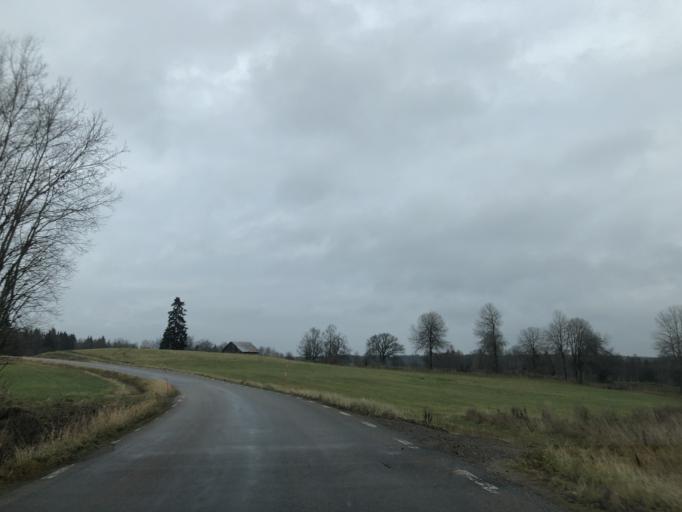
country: SE
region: Vaestra Goetaland
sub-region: Ulricehamns Kommun
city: Ulricehamn
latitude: 57.8886
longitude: 13.5118
